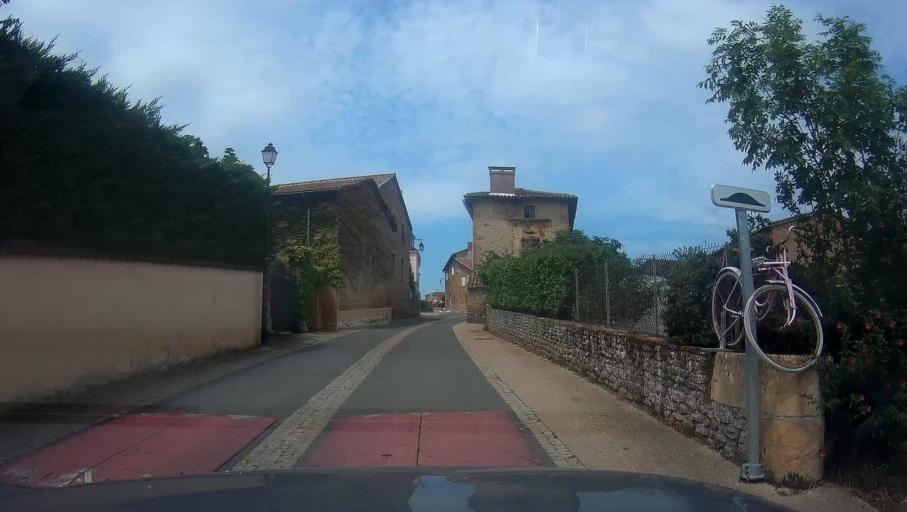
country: FR
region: Rhone-Alpes
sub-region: Departement du Rhone
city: Theize
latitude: 45.9264
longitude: 4.6045
